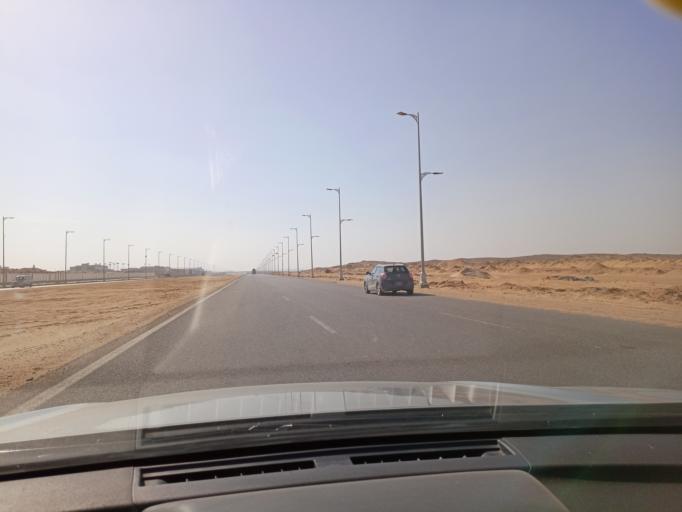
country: EG
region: Muhafazat al Qalyubiyah
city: Al Khankah
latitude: 30.0444
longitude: 31.7086
